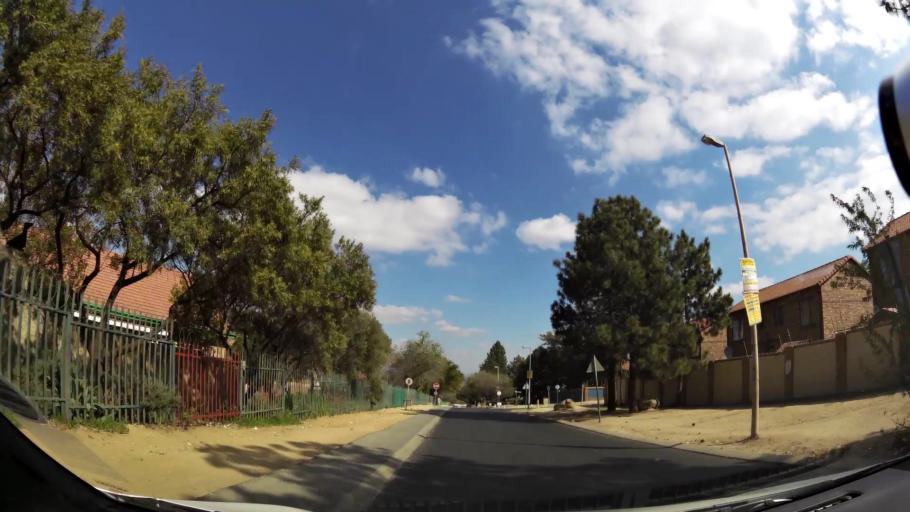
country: ZA
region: Gauteng
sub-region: City of Johannesburg Metropolitan Municipality
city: Midrand
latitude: -25.9883
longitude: 28.1166
